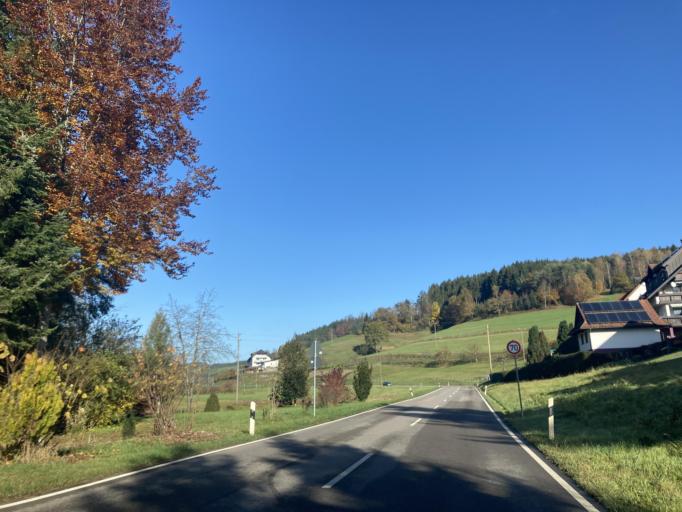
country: DE
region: Baden-Wuerttemberg
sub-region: Freiburg Region
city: Elzach
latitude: 48.1879
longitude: 8.0855
